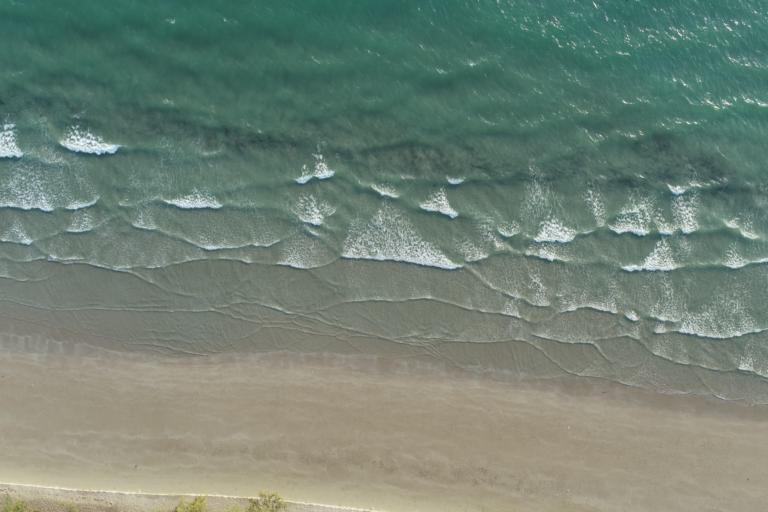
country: TH
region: Rayong
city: Rayong
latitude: 12.5997
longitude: 101.4037
